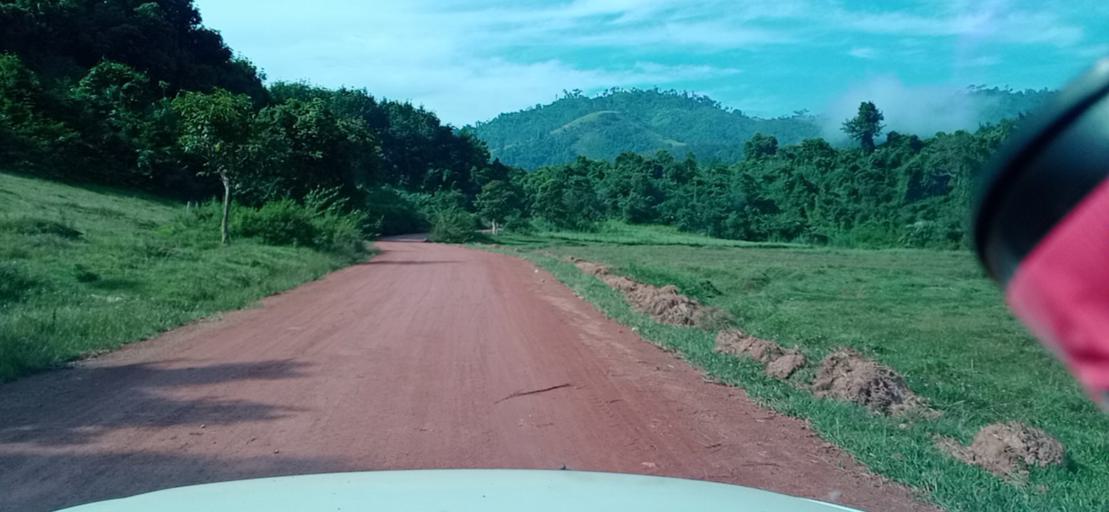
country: TH
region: Changwat Bueng Kan
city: Pak Khat
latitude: 18.6724
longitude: 103.1962
